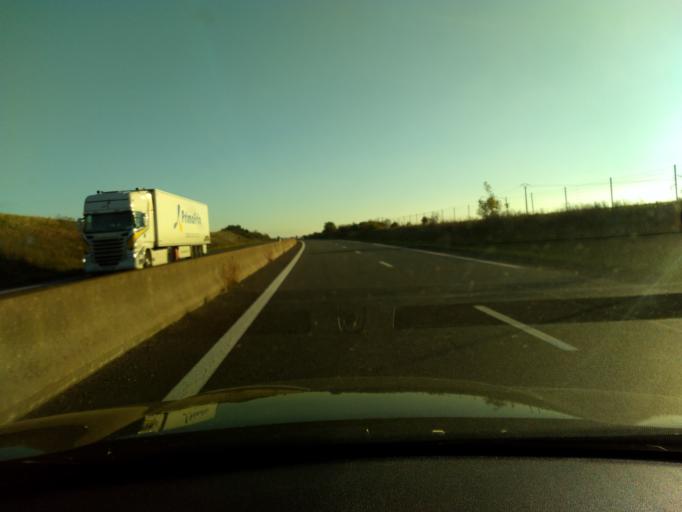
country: FR
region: Lorraine
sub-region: Departement de la Moselle
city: Fleury
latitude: 49.0537
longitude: 6.1746
